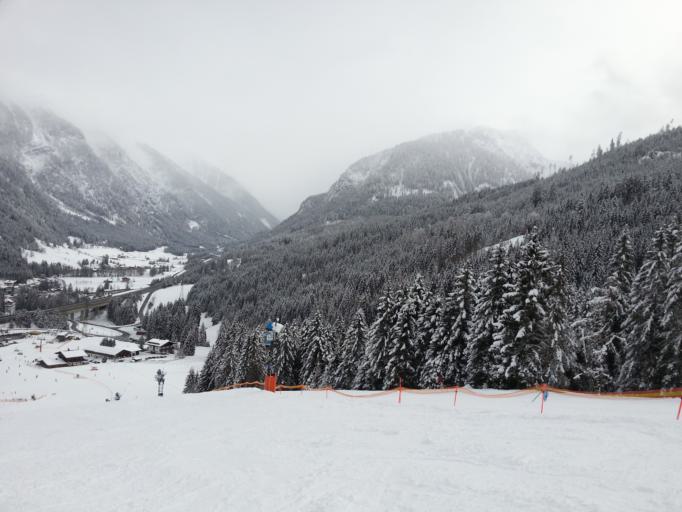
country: AT
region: Salzburg
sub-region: Politischer Bezirk Sankt Johann im Pongau
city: Flachau
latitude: 47.3003
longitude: 13.3859
